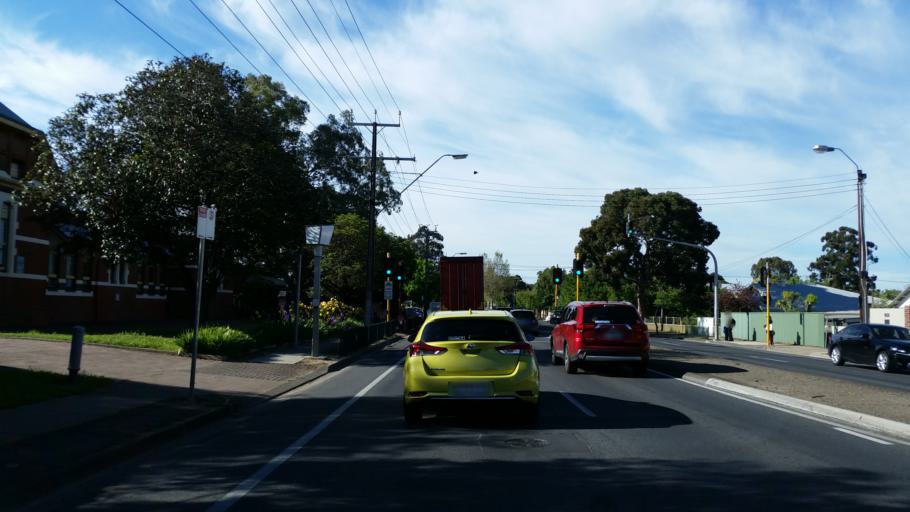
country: AU
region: South Australia
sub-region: Norwood Payneham St Peters
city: Trinity Gardens
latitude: -34.9087
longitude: 138.6401
